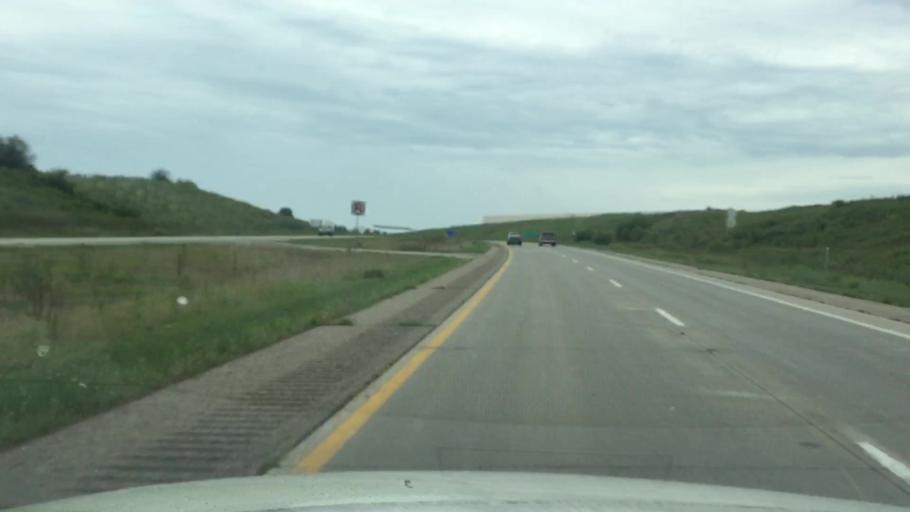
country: US
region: Iowa
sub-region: Warren County
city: Norwalk
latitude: 41.5124
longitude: -93.6550
